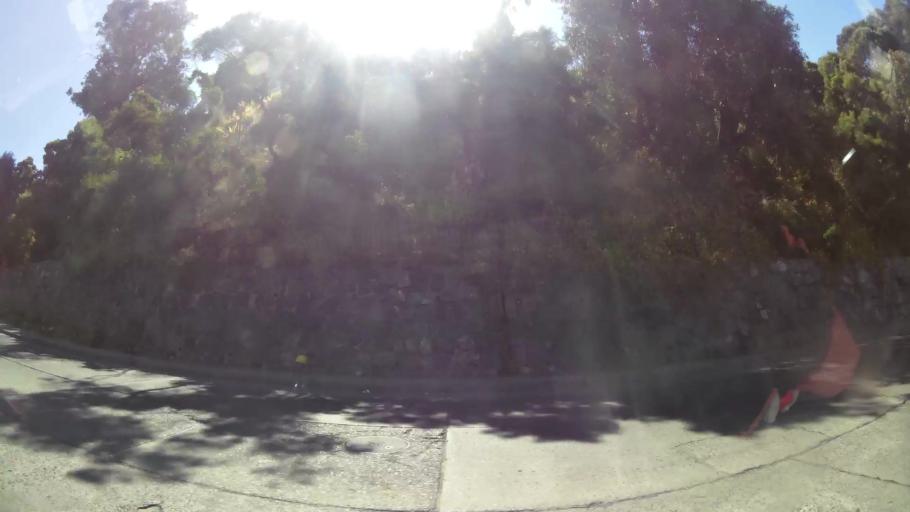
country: CL
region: Valparaiso
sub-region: Provincia de Valparaiso
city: Valparaiso
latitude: -33.0222
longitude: -71.6342
